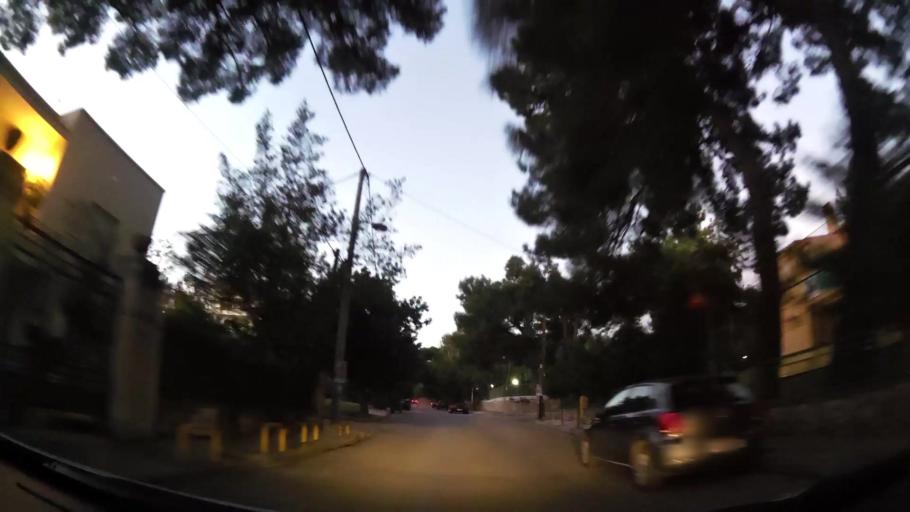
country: GR
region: Attica
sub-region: Nomarchia Athinas
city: Marousi
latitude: 38.0605
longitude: 23.8069
